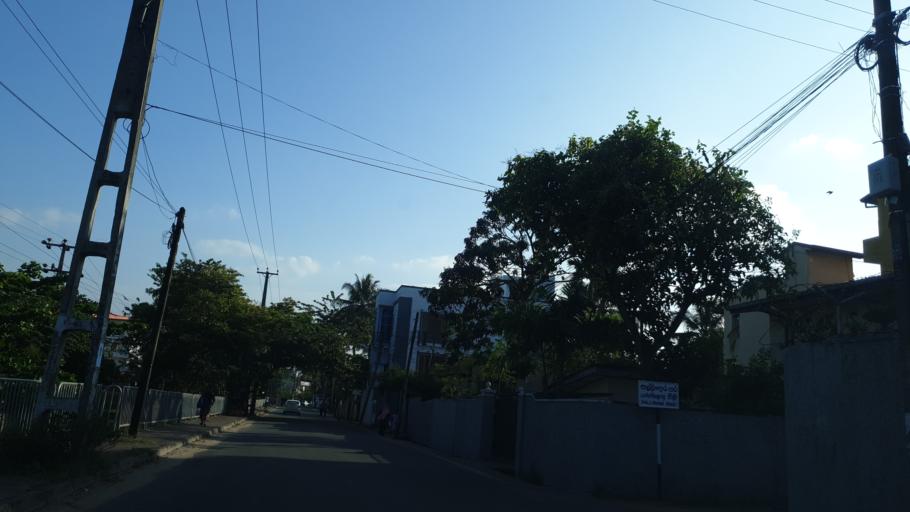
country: LK
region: Western
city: Galkissa
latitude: 6.8472
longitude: 79.8772
